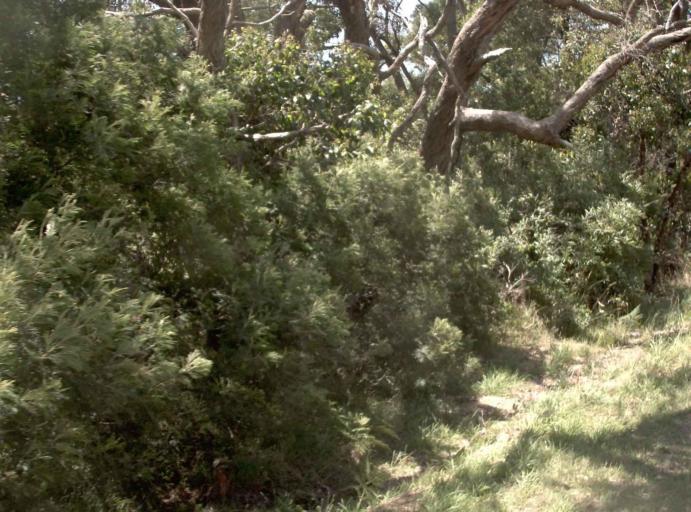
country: AU
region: Victoria
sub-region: Bass Coast
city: North Wonthaggi
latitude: -38.6680
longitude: 145.8603
